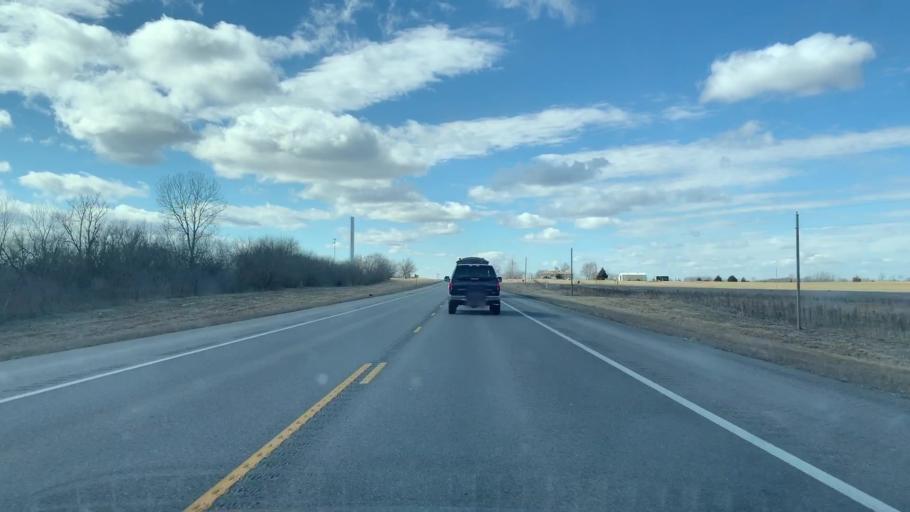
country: US
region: Kansas
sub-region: Cherokee County
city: Columbus
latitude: 37.3400
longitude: -94.9011
